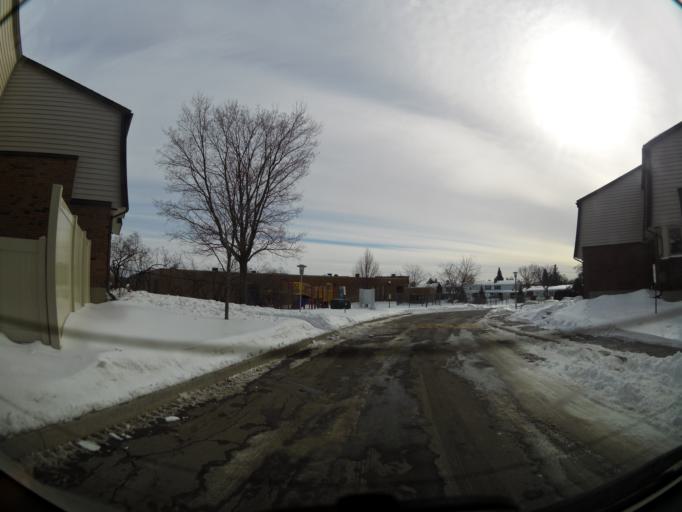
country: CA
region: Ontario
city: Ottawa
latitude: 45.4441
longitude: -75.6004
